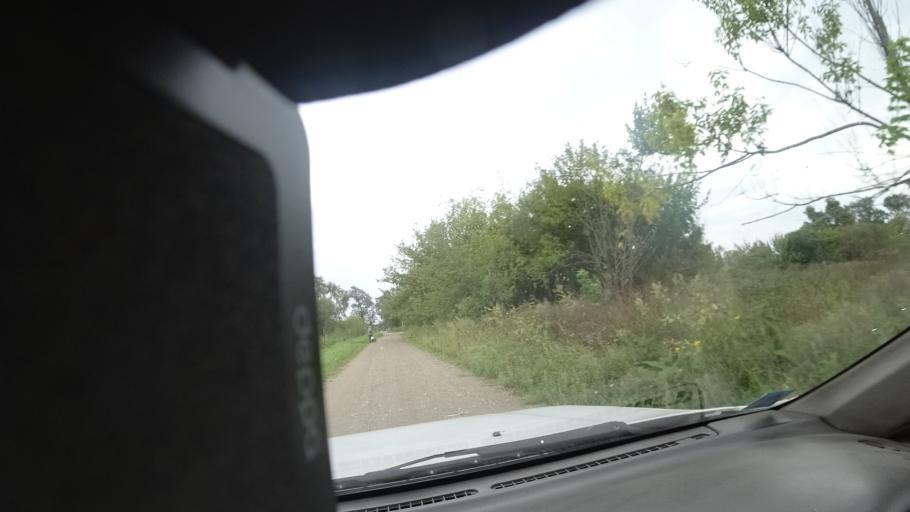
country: RU
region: Primorskiy
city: Lazo
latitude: 45.8298
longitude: 133.6148
